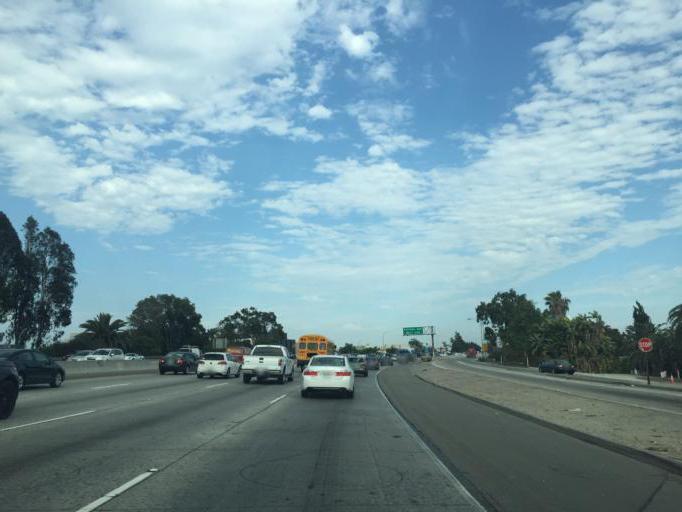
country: US
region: California
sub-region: Los Angeles County
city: Culver City
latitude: 34.0367
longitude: -118.3797
